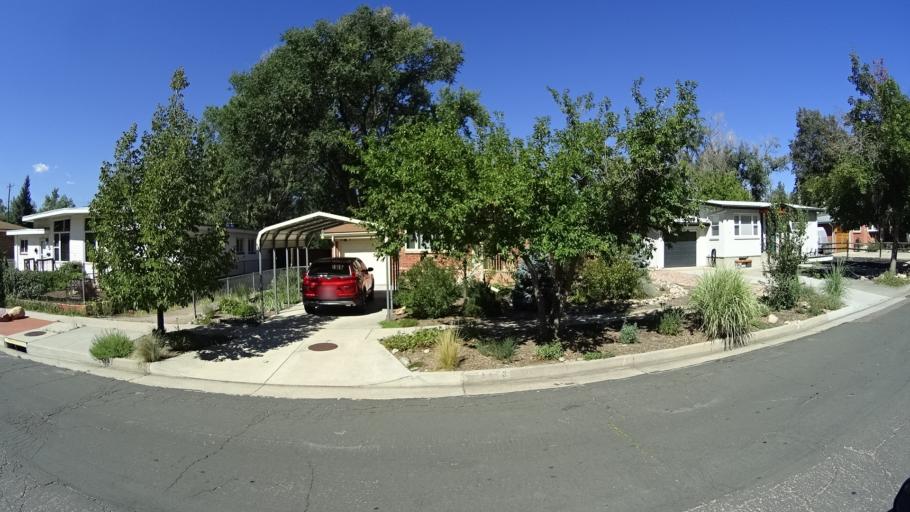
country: US
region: Colorado
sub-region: El Paso County
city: Colorado Springs
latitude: 38.8534
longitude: -104.8060
